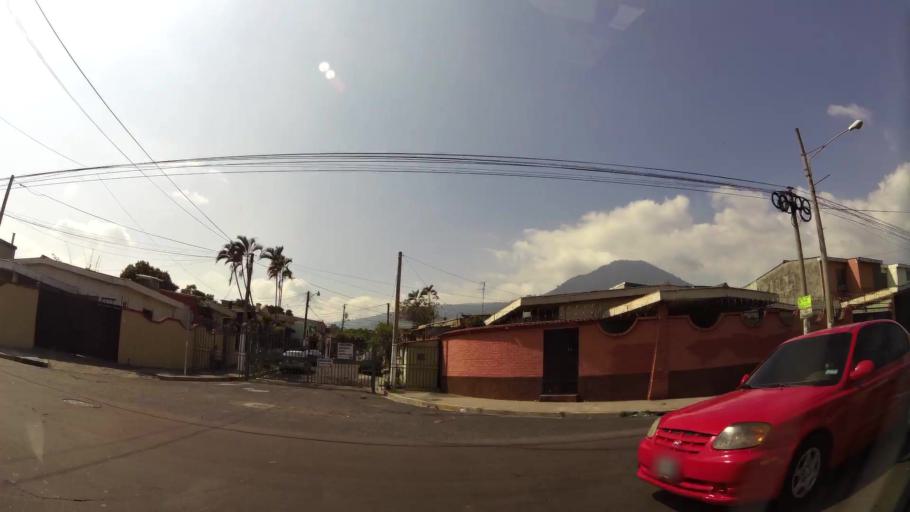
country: SV
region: San Salvador
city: Mejicanos
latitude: 13.7220
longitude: -89.2168
